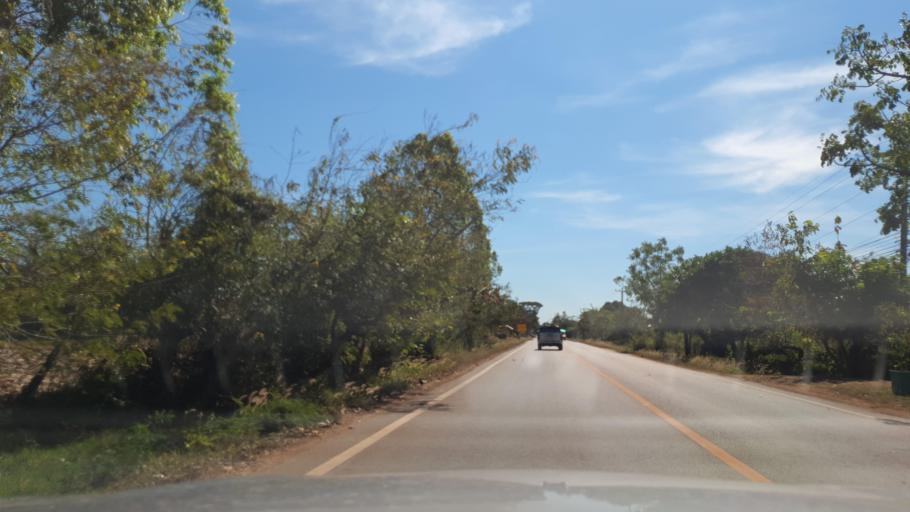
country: TH
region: Sakon Nakhon
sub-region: Amphoe Khok Si Suphan
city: Khok Si Suphan
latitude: 17.0602
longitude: 104.2138
